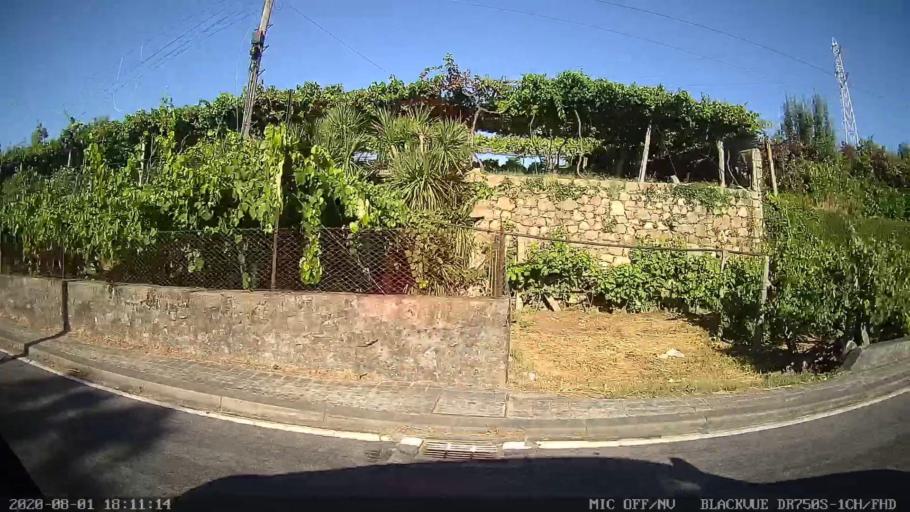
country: PT
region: Porto
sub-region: Santo Tirso
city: Sao Miguel do Couto
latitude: 41.3002
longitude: -8.4709
